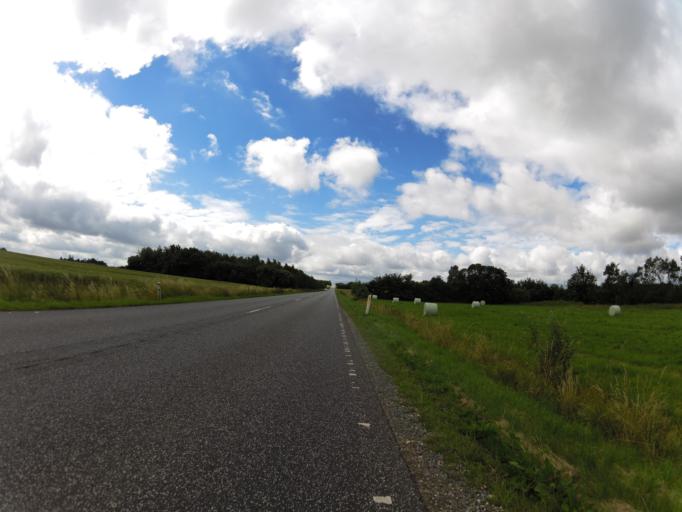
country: DK
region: North Denmark
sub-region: Mariagerfjord Kommune
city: Hadsund
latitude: 56.6047
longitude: 10.1454
